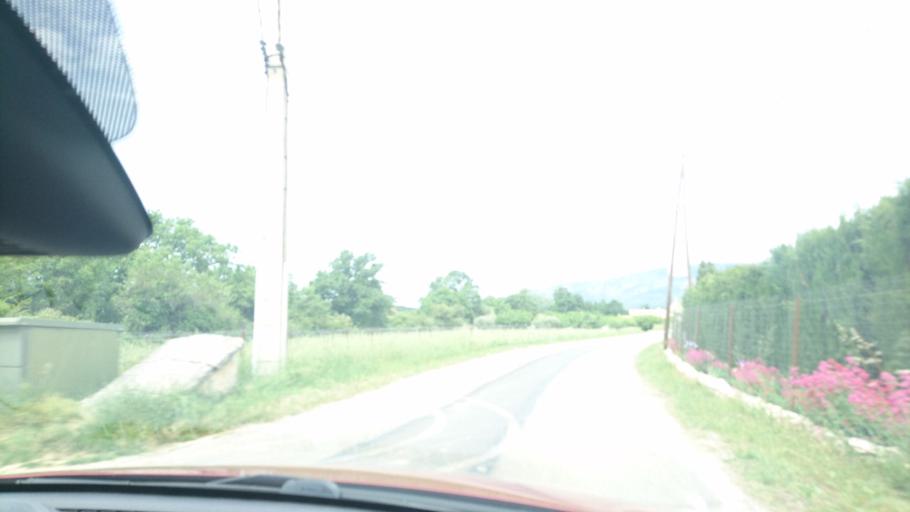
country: FR
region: Provence-Alpes-Cote d'Azur
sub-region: Departement du Vaucluse
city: Villes-sur-Auzon
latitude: 44.0695
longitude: 5.2326
